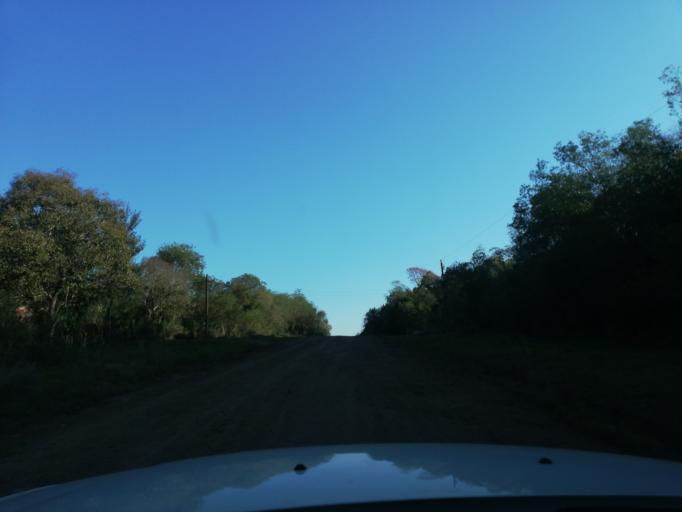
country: AR
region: Misiones
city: Cerro Cora
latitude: -27.5940
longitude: -55.6944
